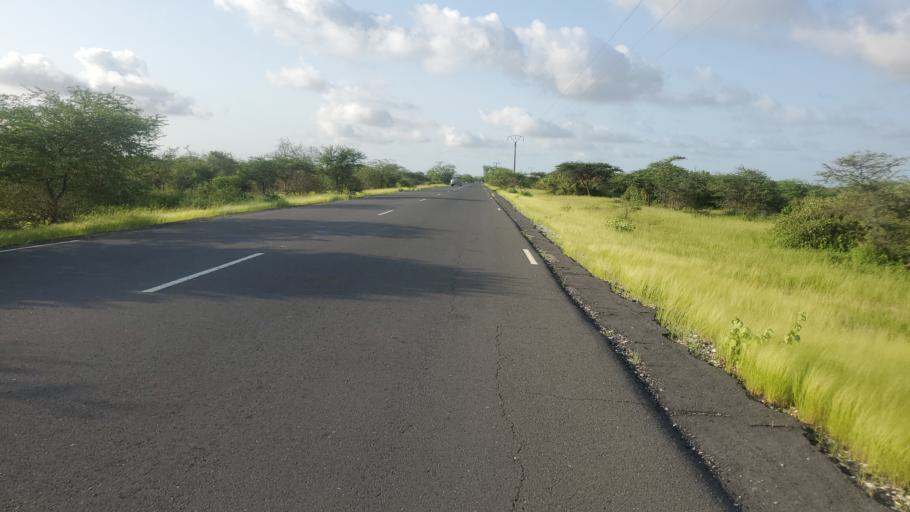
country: SN
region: Saint-Louis
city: Saint-Louis
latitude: 16.1155
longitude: -16.4136
